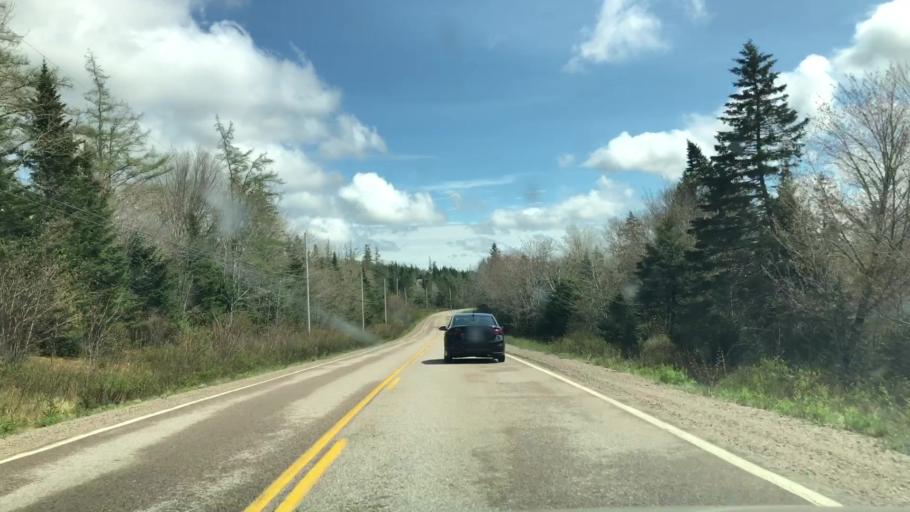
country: CA
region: Nova Scotia
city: Antigonish
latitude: 45.2125
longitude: -62.0051
